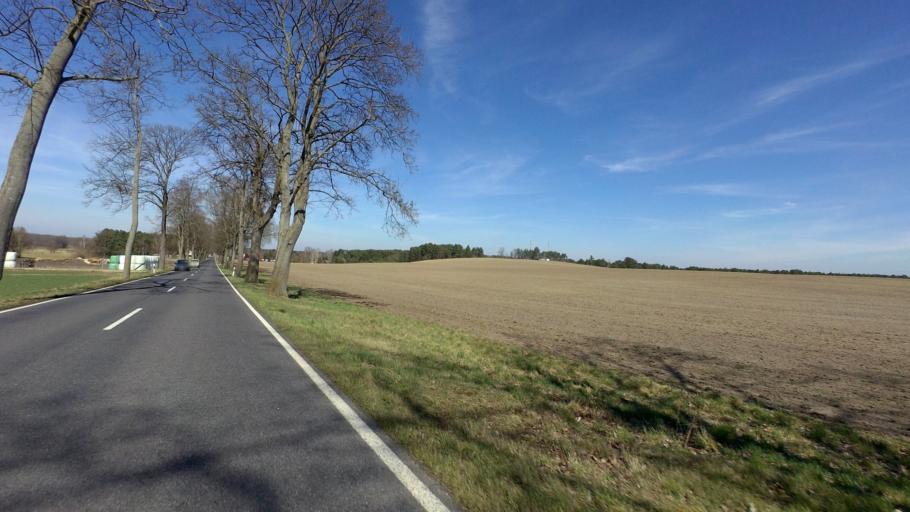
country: DE
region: Brandenburg
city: Storkow
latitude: 52.1867
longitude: 13.9184
